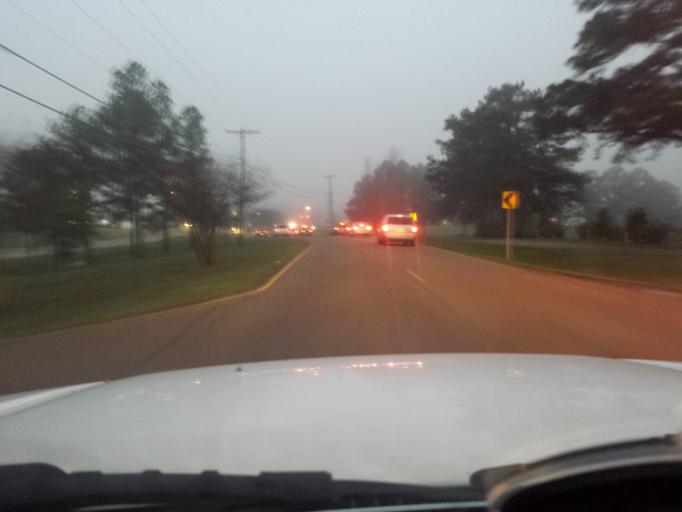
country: US
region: Mississippi
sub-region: Madison County
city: Ridgeland
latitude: 32.3856
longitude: -90.0392
